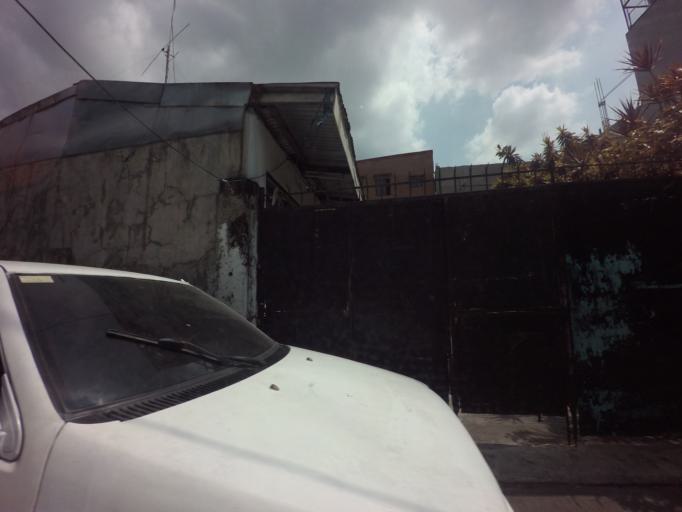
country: PH
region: Metro Manila
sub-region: Makati City
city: Makati City
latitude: 14.5700
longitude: 121.0204
